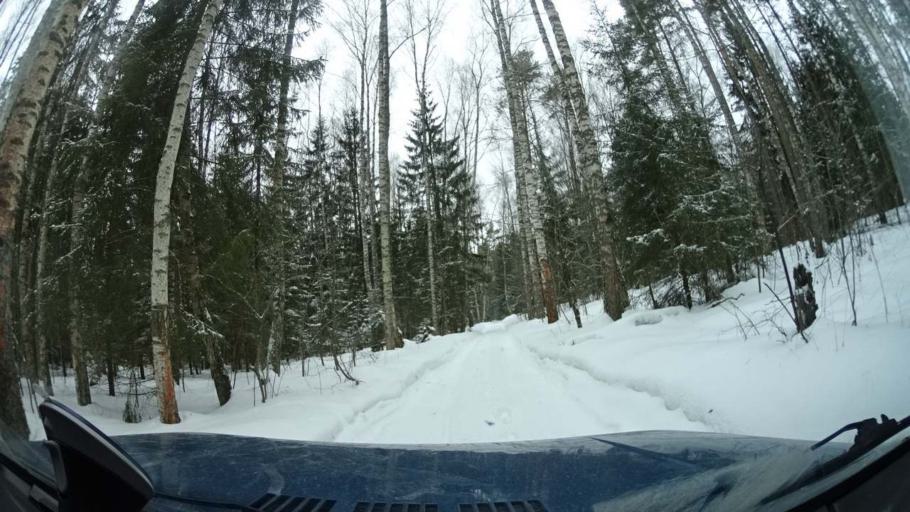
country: RU
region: Tverskaya
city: Radchenko
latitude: 56.6783
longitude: 36.4519
